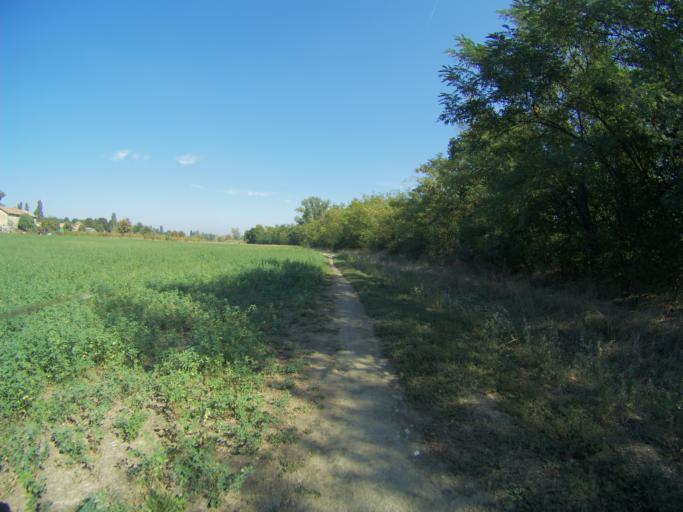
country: IT
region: Emilia-Romagna
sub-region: Provincia di Reggio Emilia
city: Forche
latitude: 44.6280
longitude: 10.5756
